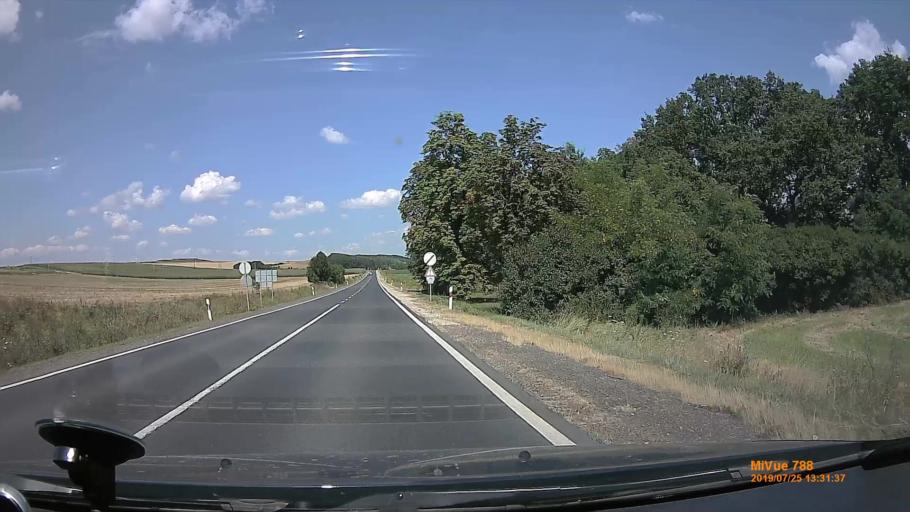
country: HU
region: Borsod-Abauj-Zemplen
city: Encs
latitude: 48.3658
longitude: 21.1404
